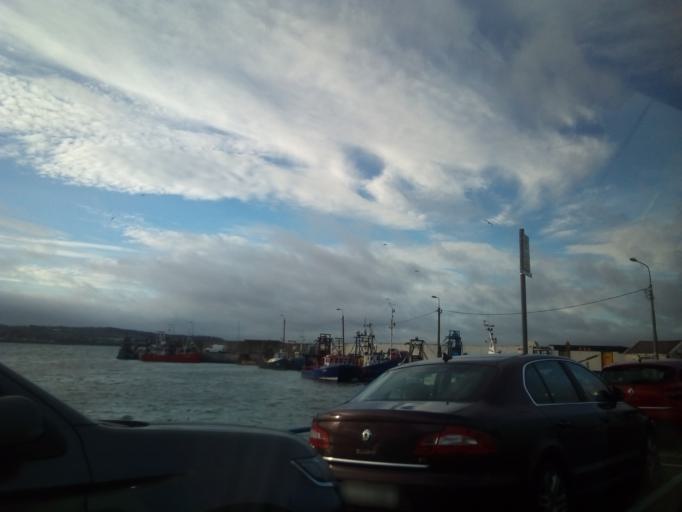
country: IE
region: Leinster
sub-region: Fingal County
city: Skerries
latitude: 53.5850
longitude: -6.1051
